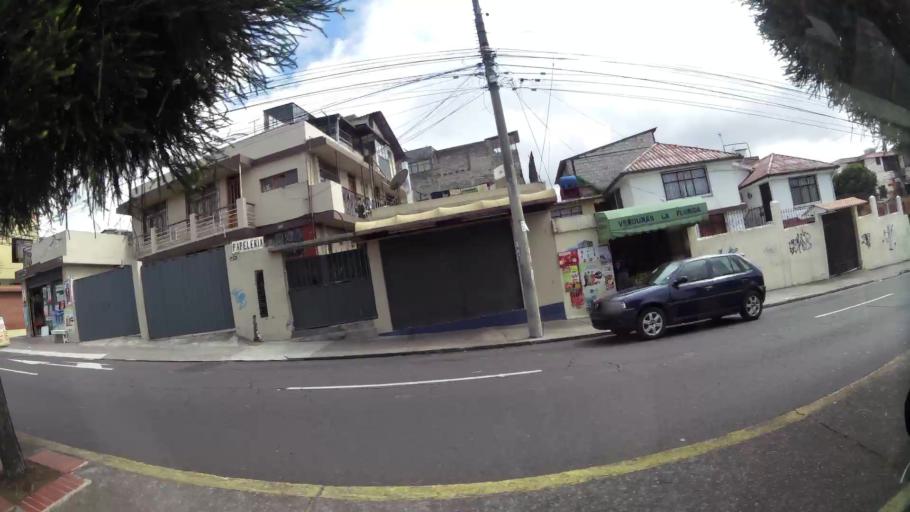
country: EC
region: Pichincha
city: Quito
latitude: -0.1437
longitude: -78.4969
